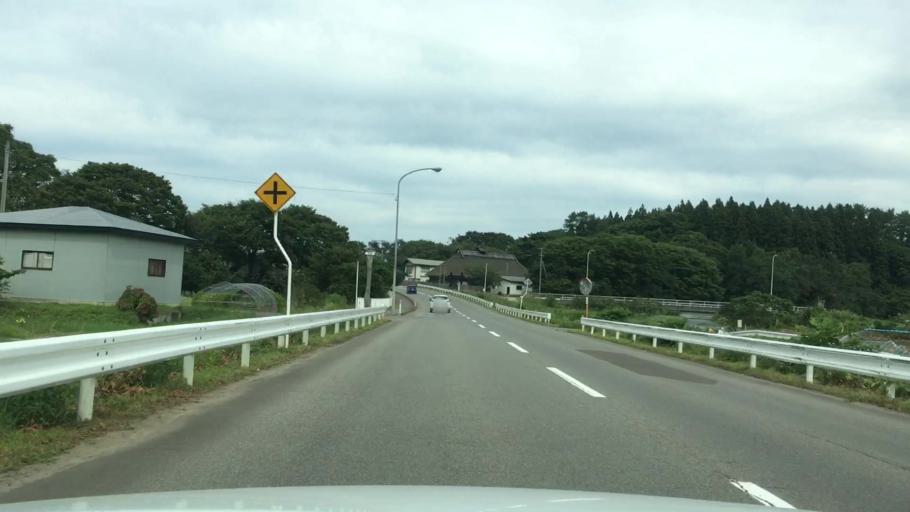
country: JP
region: Aomori
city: Shimokizukuri
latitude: 40.7561
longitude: 140.2307
